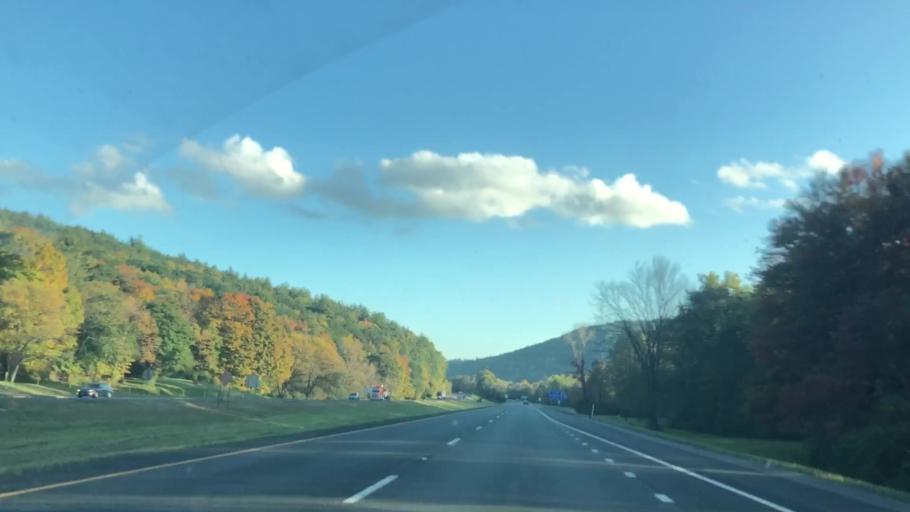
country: US
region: Massachusetts
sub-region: Franklin County
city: Bernardston
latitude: 42.7162
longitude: -72.5667
